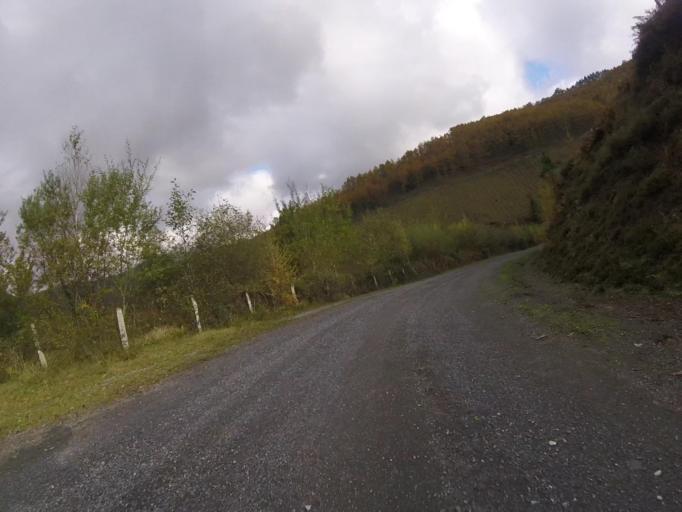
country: ES
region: Navarre
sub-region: Provincia de Navarra
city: Goizueta
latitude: 43.2138
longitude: -1.8325
